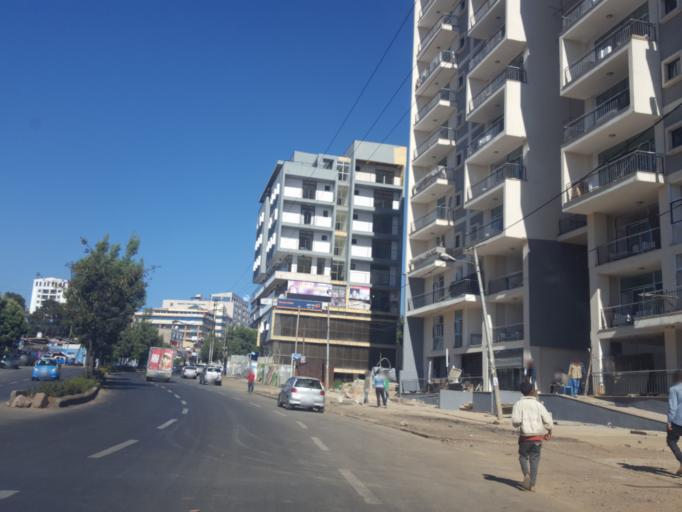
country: ET
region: Adis Abeba
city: Addis Ababa
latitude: 9.0579
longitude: 38.7397
